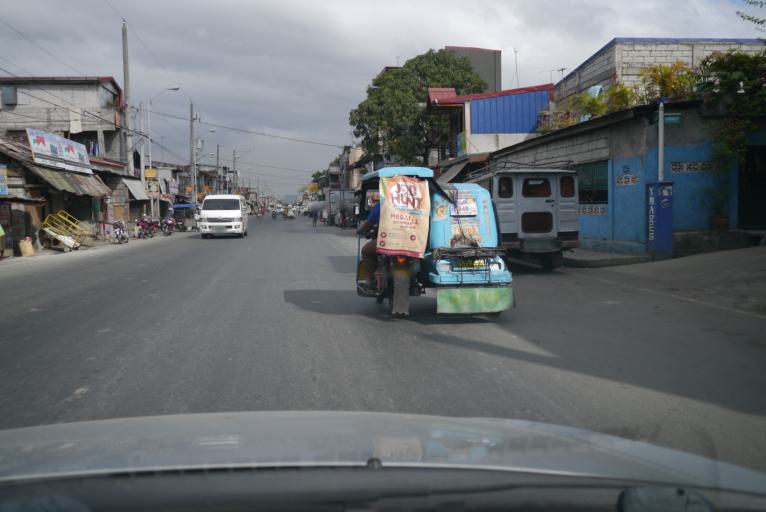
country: PH
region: Calabarzon
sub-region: Province of Rizal
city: Taytay
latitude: 14.5535
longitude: 121.1177
